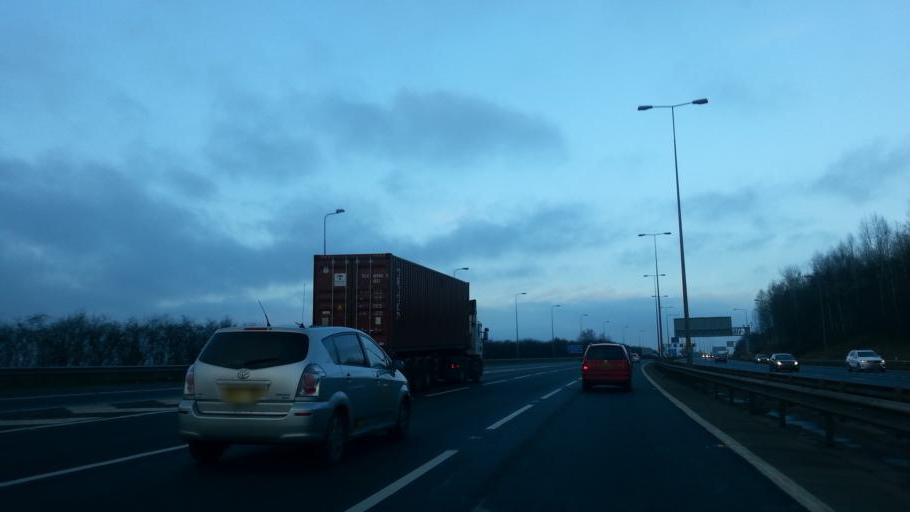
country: GB
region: England
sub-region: Worcestershire
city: Fernhill Heath
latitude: 52.2162
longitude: -2.1555
